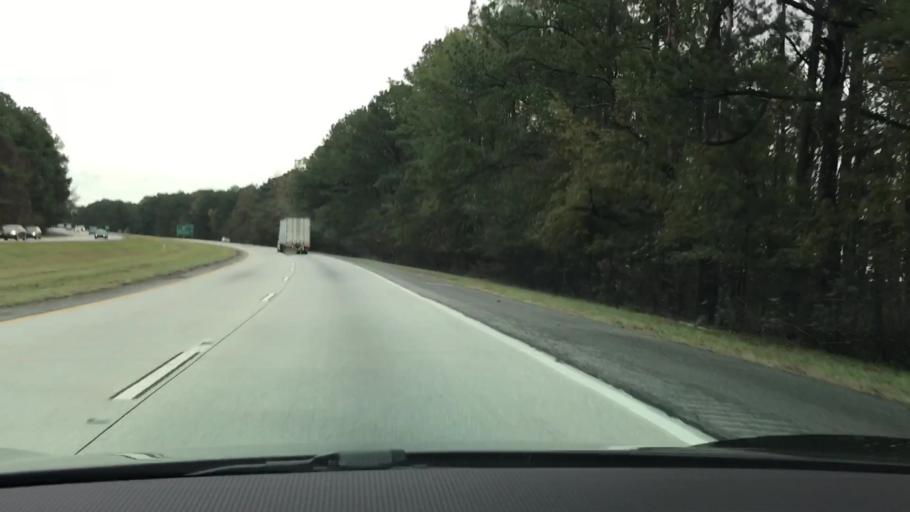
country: US
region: Georgia
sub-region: Taliaferro County
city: Crawfordville
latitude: 33.4980
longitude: -82.8149
